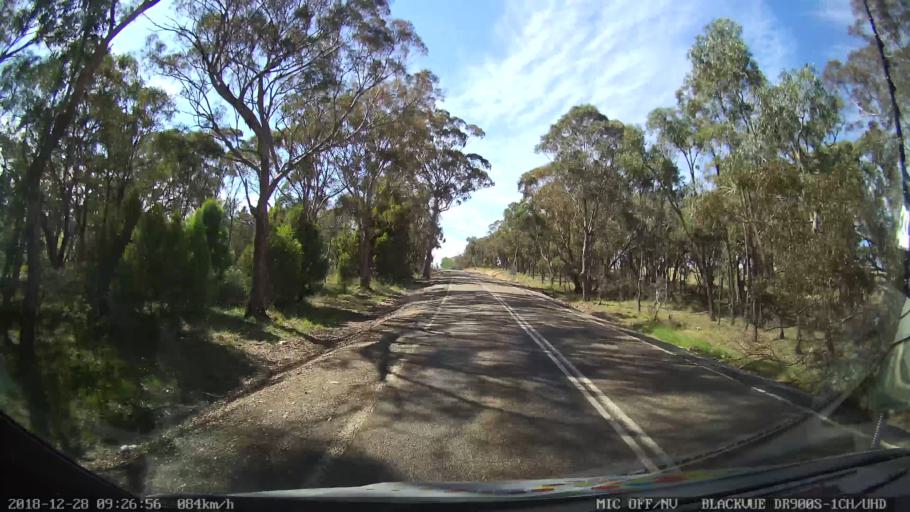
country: AU
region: New South Wales
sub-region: Upper Lachlan Shire
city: Crookwell
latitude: -34.4239
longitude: 149.4047
